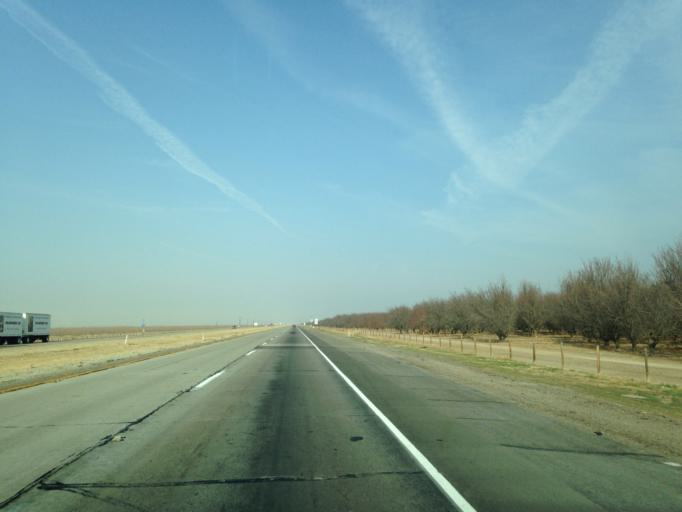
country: US
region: California
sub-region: Kern County
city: Buttonwillow
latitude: 35.5034
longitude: -119.5383
